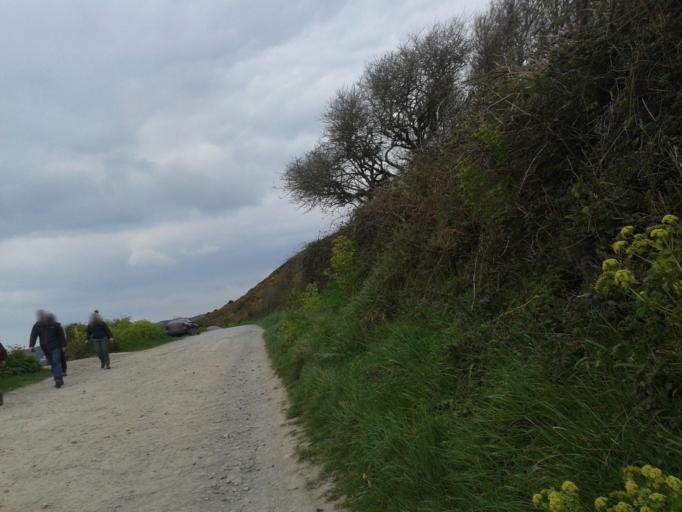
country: GB
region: England
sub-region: Devon
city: Braunton
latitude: 51.1551
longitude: -4.2113
